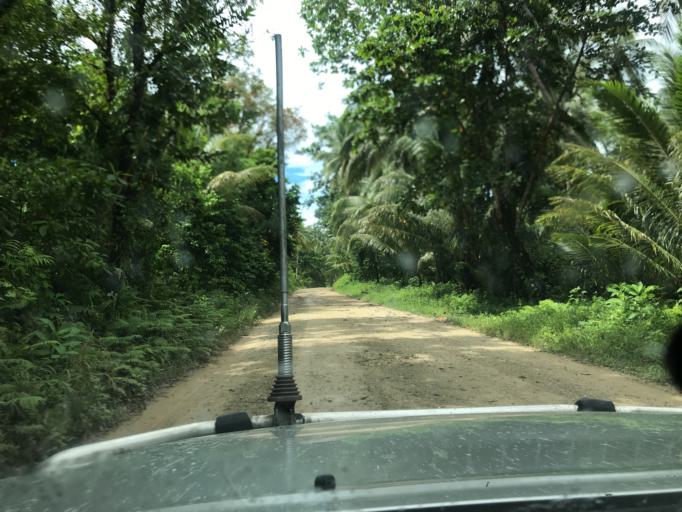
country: SB
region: Malaita
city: Auki
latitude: -8.3548
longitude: 160.6537
